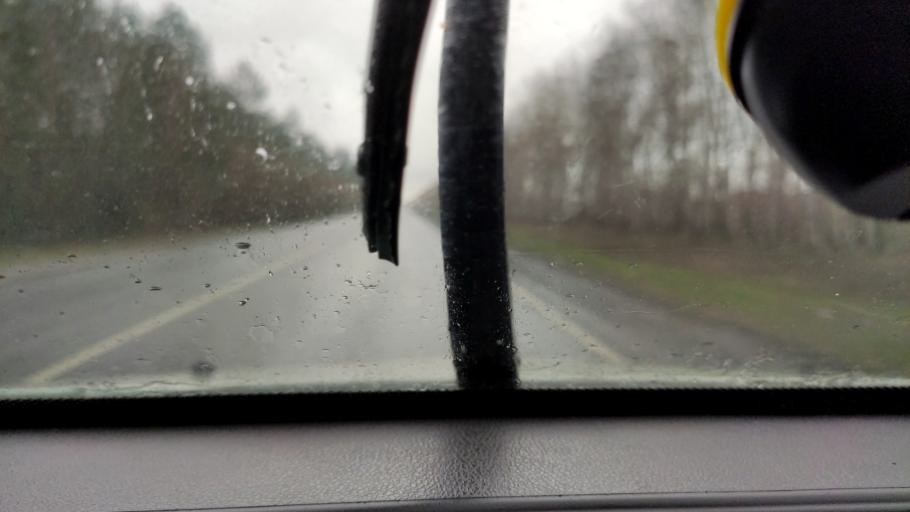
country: RU
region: Samara
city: Povolzhskiy
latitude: 53.6113
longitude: 49.6188
